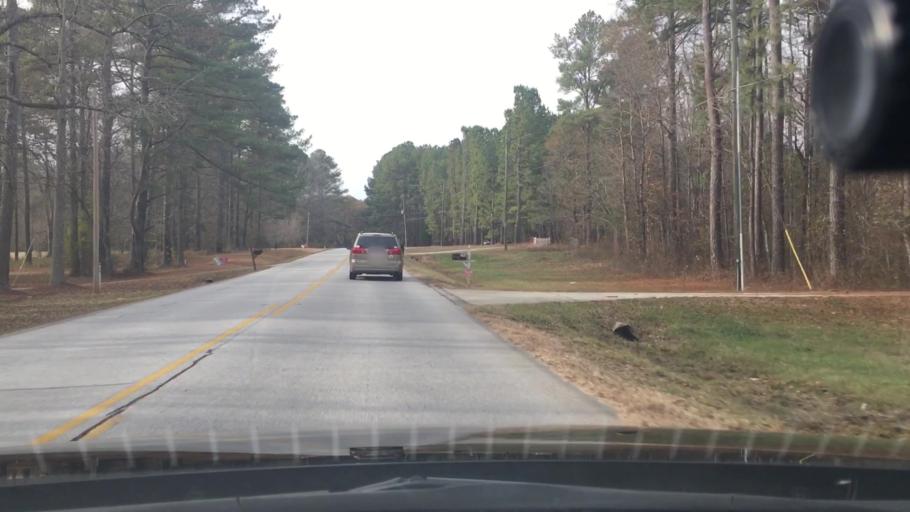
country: US
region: Georgia
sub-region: Coweta County
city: Senoia
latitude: 33.3268
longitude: -84.5009
